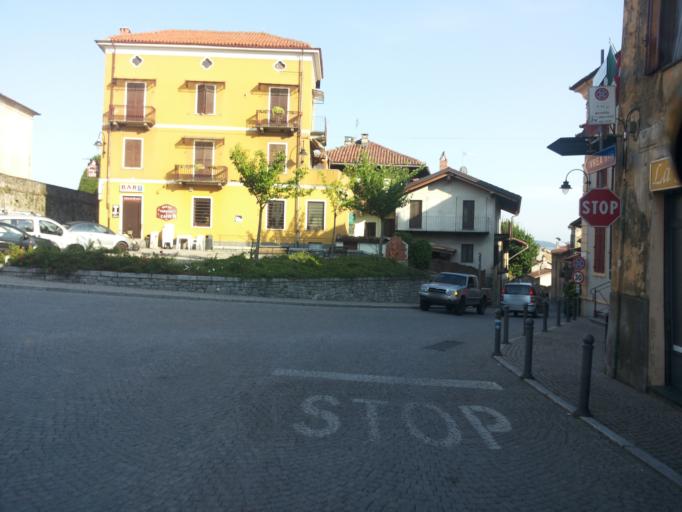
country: IT
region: Piedmont
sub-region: Provincia di Torino
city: Piverone
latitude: 45.4478
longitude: 8.0070
